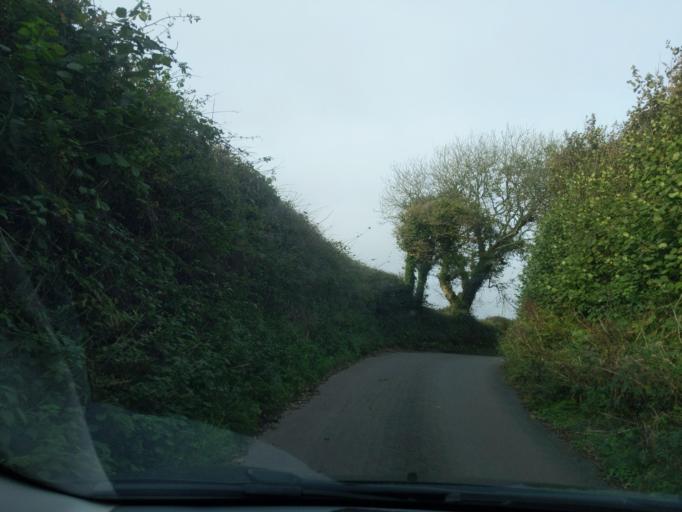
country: GB
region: England
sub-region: Cornwall
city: Looe
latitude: 50.3710
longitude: -4.4163
